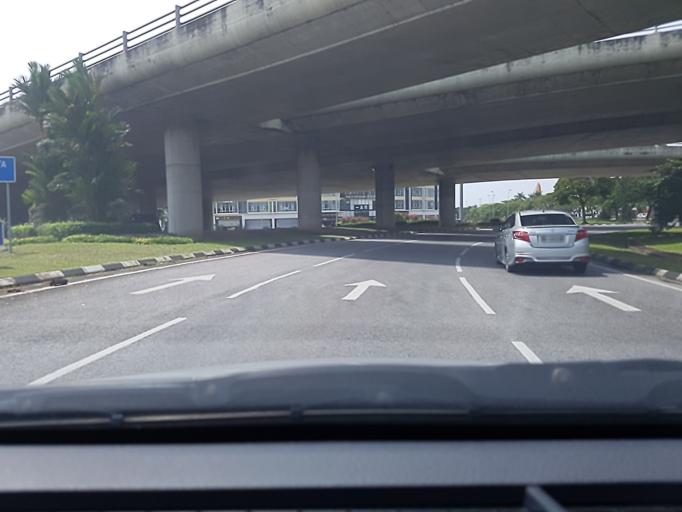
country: MY
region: Sarawak
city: Kuching
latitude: 1.5049
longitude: 110.3482
